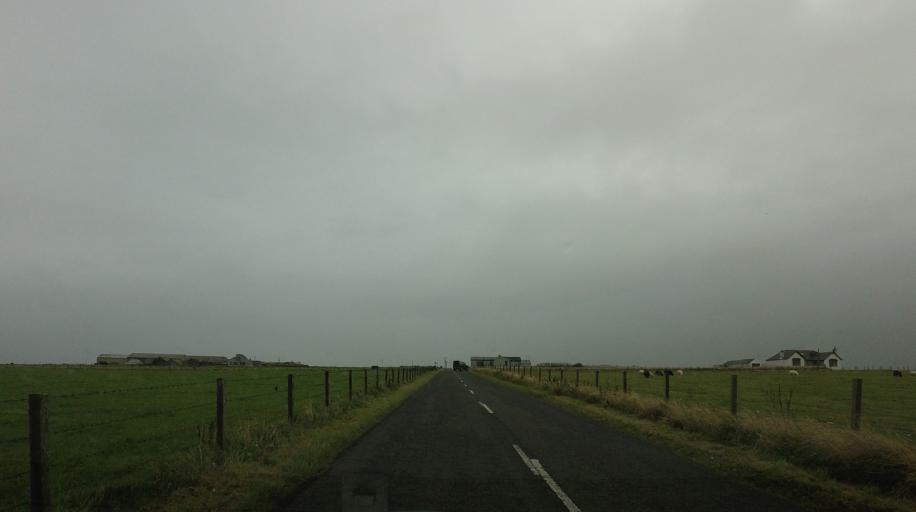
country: GB
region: Scotland
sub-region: Orkney Islands
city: Stromness
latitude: 59.1313
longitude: -3.3058
